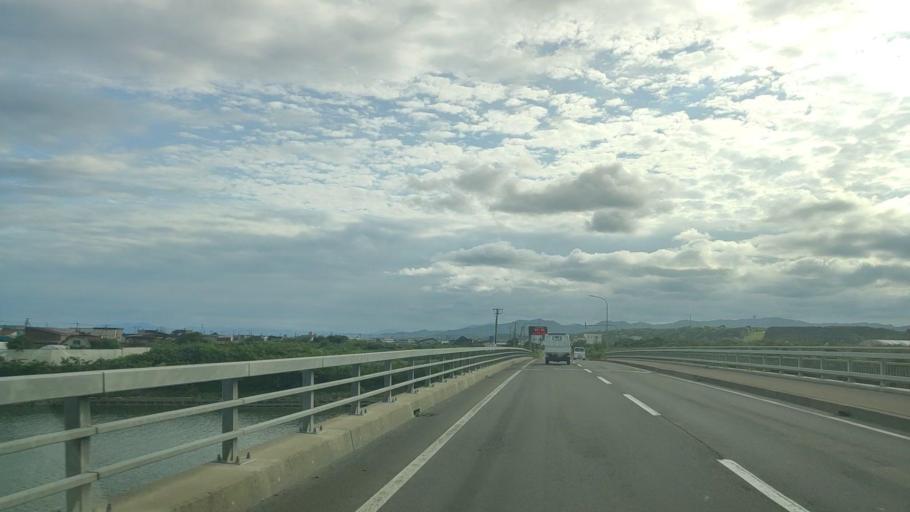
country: JP
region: Hokkaido
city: Niseko Town
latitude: 42.5240
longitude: 140.3881
